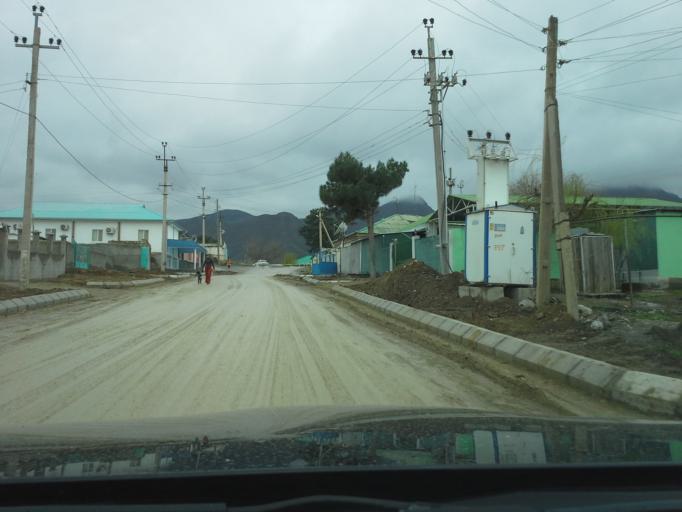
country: TM
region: Ahal
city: Abadan
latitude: 37.9572
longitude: 58.2075
